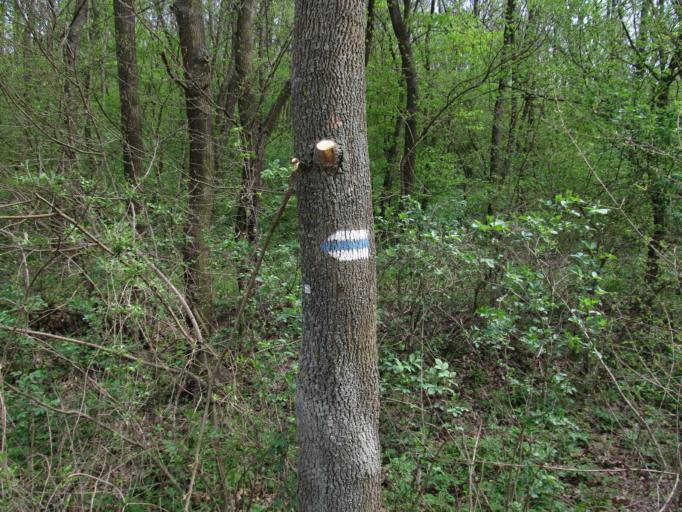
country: HU
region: Pest
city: Piliscsaba
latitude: 47.6135
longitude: 18.8324
